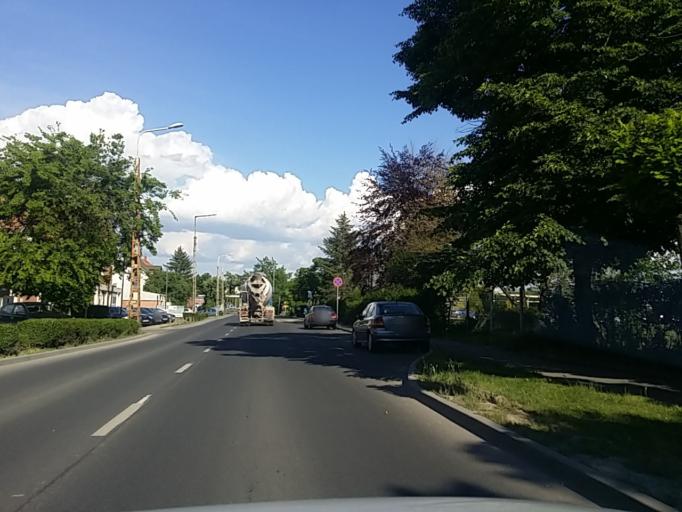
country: HU
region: Budapest
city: Budapest III. keruelet
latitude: 47.5603
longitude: 19.0321
